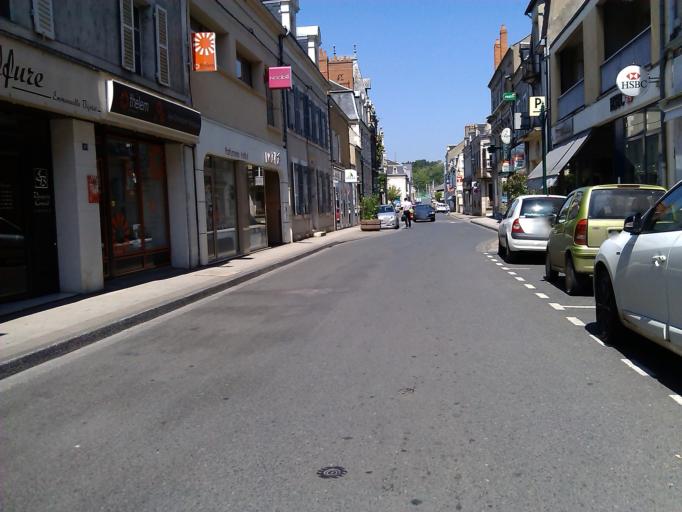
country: FR
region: Centre
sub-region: Departement de l'Indre
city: Argenton-sur-Creuse
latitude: 46.5900
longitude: 1.5183
